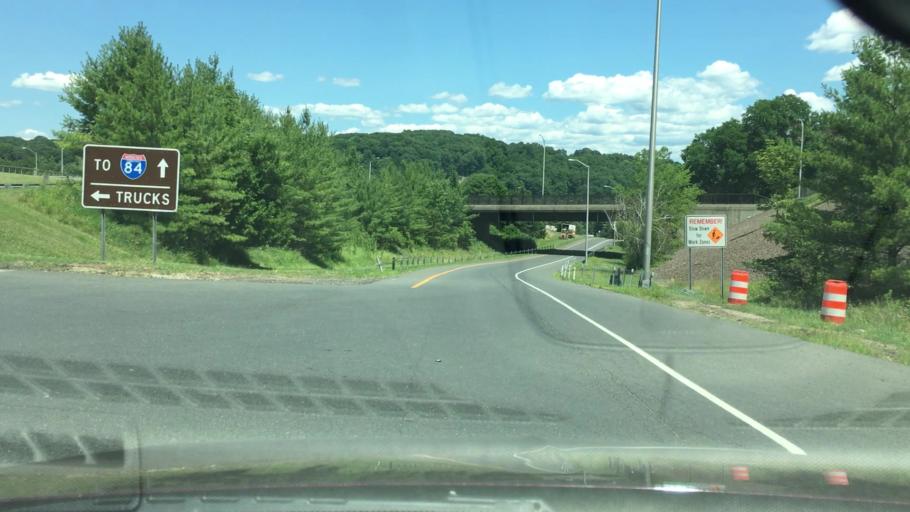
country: US
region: New York
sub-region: Putnam County
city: Peach Lake
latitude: 41.3884
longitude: -73.5180
